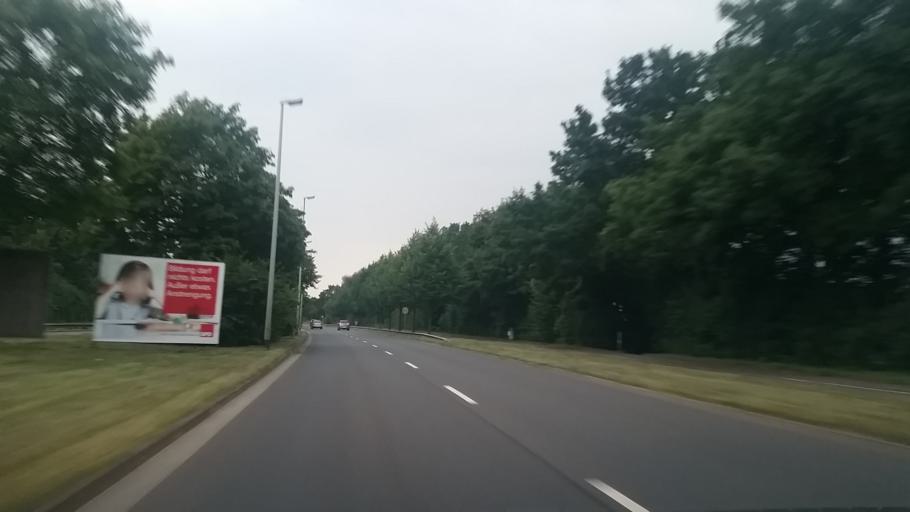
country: DE
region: Lower Saxony
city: Hannover
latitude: 52.3587
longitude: 9.7044
